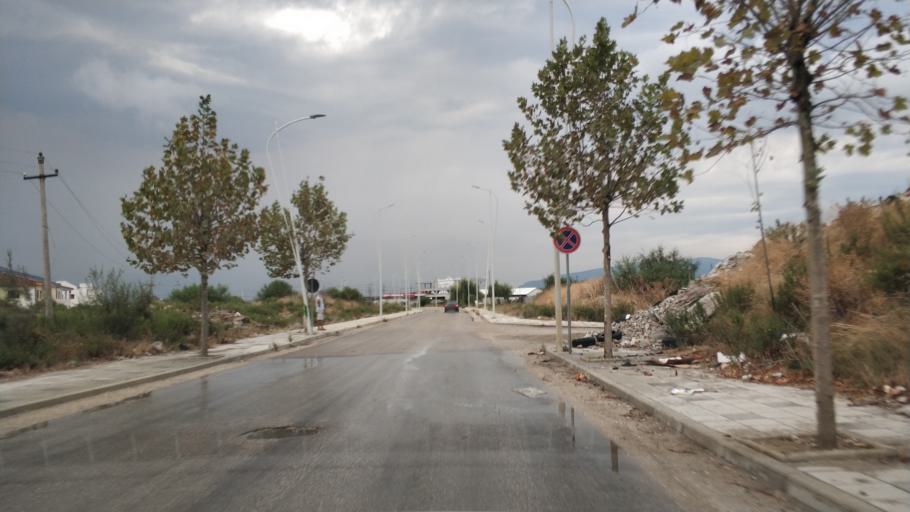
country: AL
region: Vlore
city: Vlore
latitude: 40.4837
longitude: 19.4672
